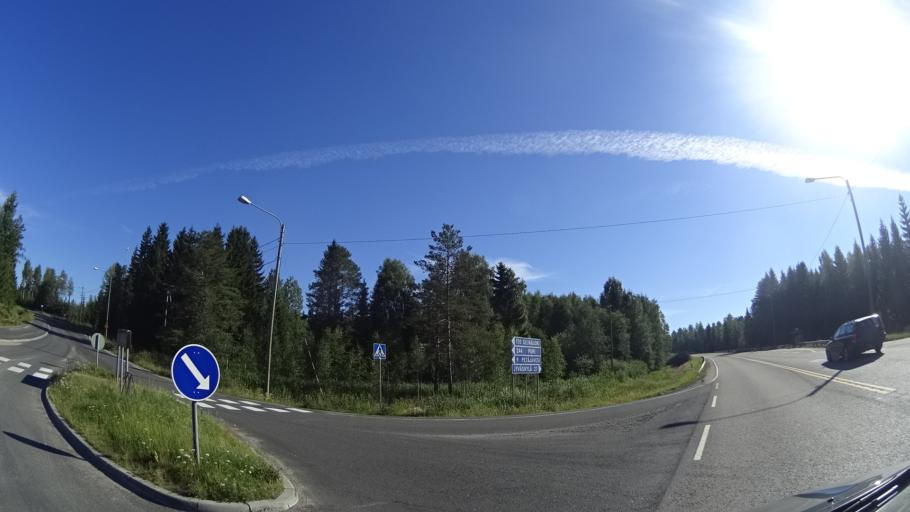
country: FI
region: Central Finland
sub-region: Jyvaeskylae
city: Petaejaevesi
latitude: 62.2706
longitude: 25.3399
